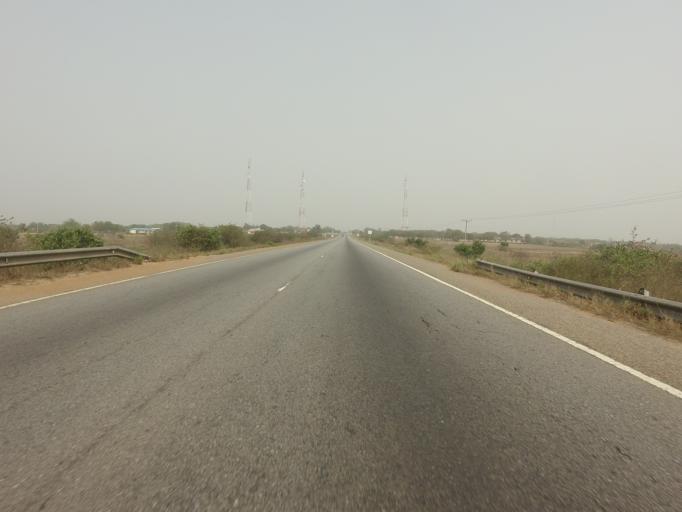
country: GH
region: Greater Accra
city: Tema
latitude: 5.8635
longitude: 0.2840
